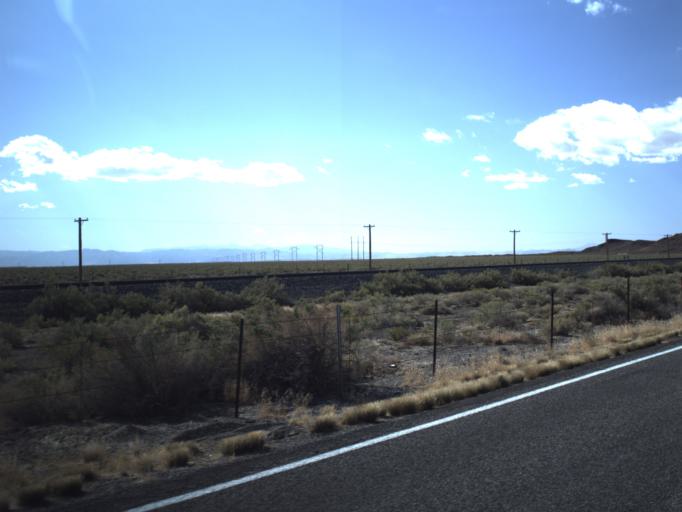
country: US
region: Utah
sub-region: Millard County
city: Delta
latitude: 39.1581
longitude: -112.7142
